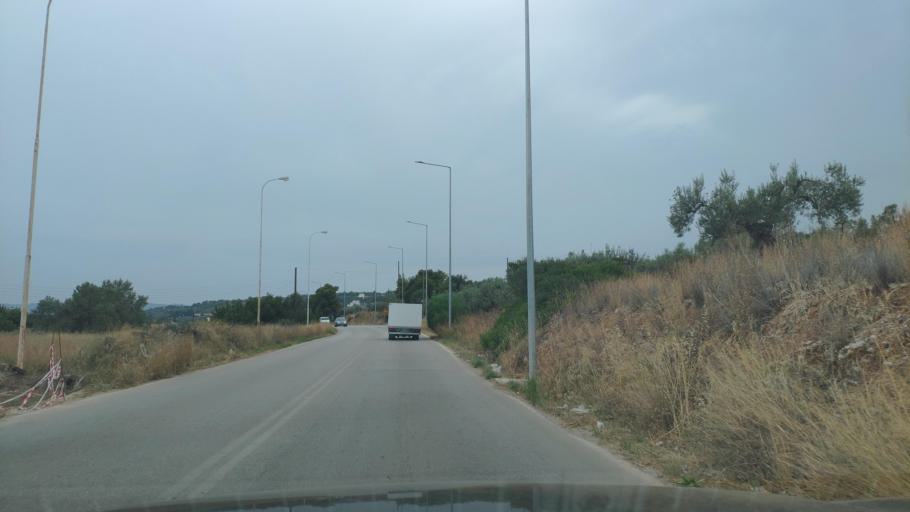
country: GR
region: Peloponnese
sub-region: Nomos Argolidos
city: Kranidi
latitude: 37.3563
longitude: 23.1598
